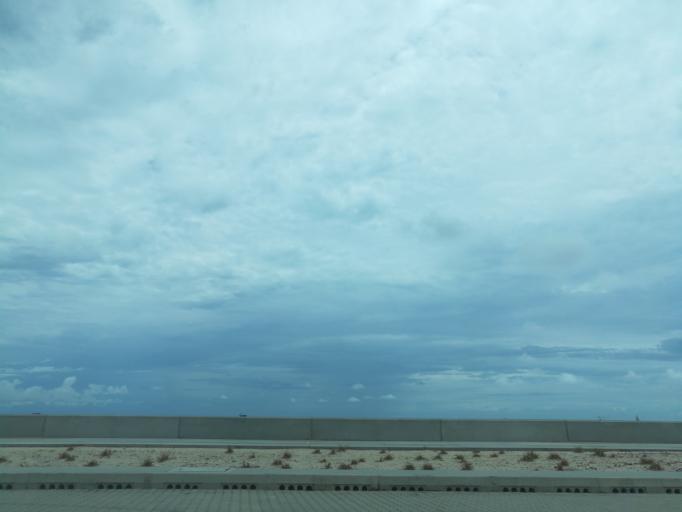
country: NG
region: Lagos
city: Ikoyi
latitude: 6.4037
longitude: 3.4148
